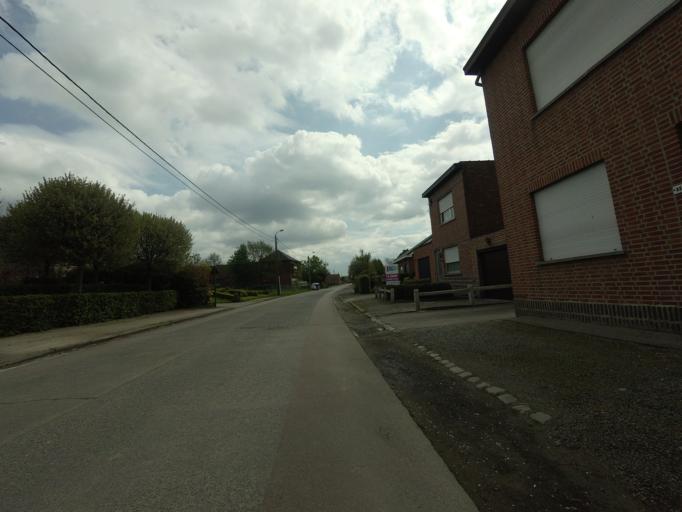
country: BE
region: Flanders
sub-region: Provincie Vlaams-Brabant
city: Zemst
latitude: 51.0122
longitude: 4.4216
